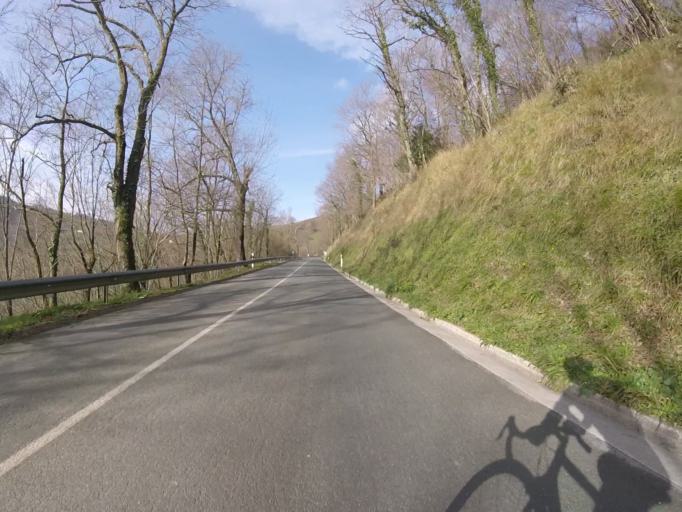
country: ES
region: Basque Country
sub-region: Provincia de Guipuzcoa
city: Asteasu
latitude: 43.2035
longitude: -2.1213
